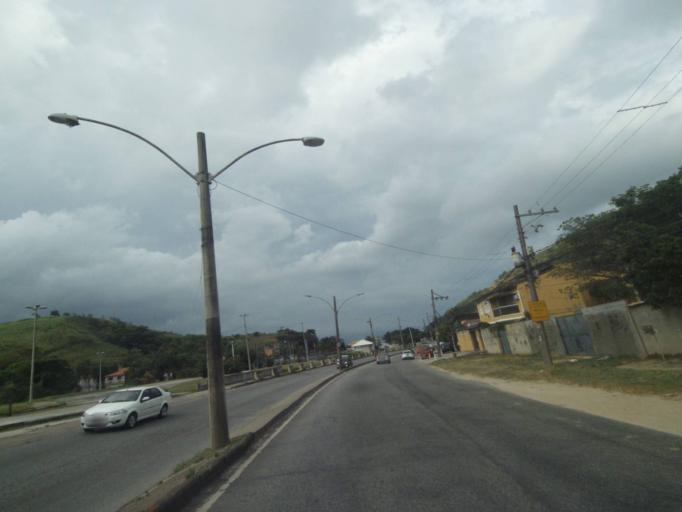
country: BR
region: Rio de Janeiro
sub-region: Nilopolis
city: Nilopolis
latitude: -22.8941
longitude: -43.3972
